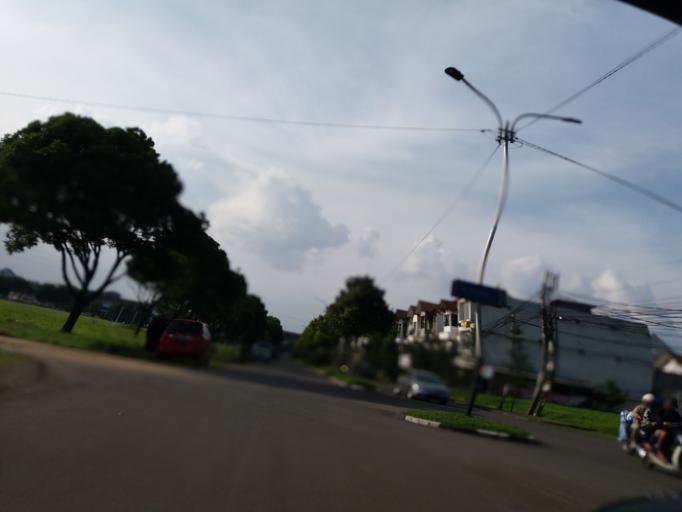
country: ID
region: West Java
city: Bandung
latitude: -6.9568
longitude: 107.6282
